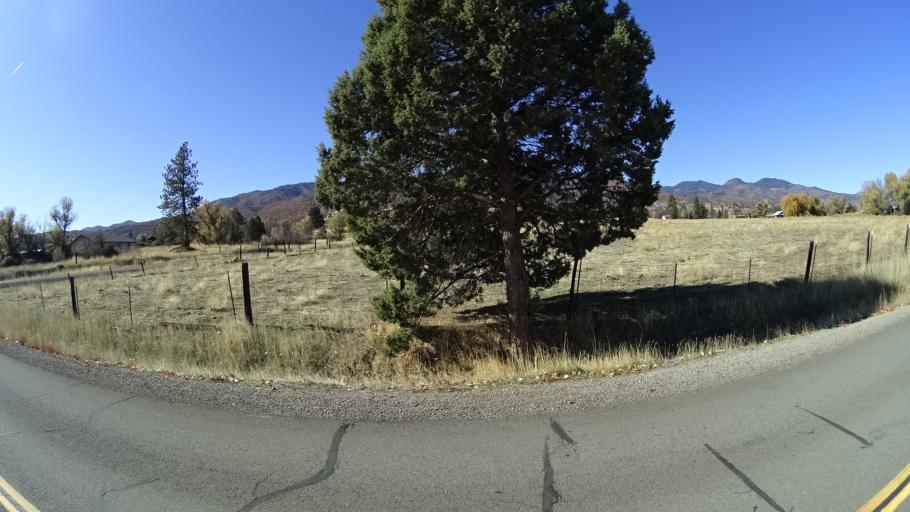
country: US
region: California
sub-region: Siskiyou County
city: Montague
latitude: 41.8997
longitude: -122.5516
